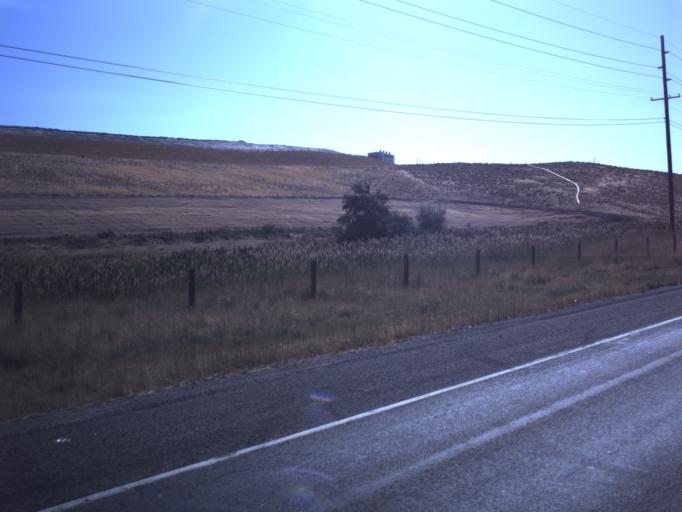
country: US
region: Utah
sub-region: Salt Lake County
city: Magna
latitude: 40.7358
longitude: -112.1720
